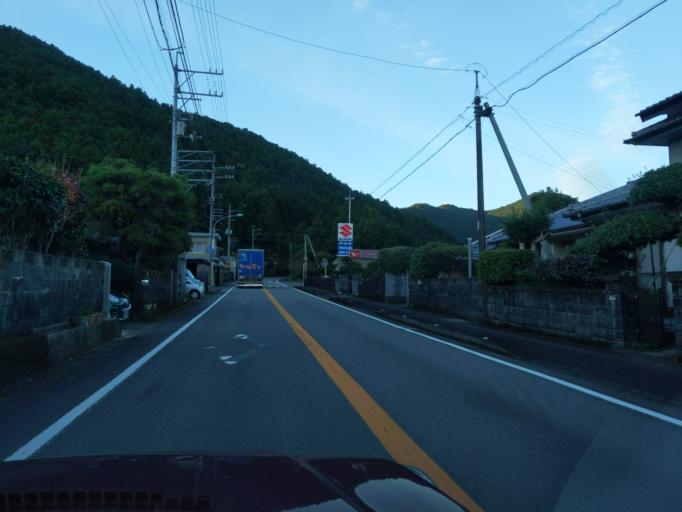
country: JP
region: Tokushima
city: Anan
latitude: 33.6892
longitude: 134.4266
